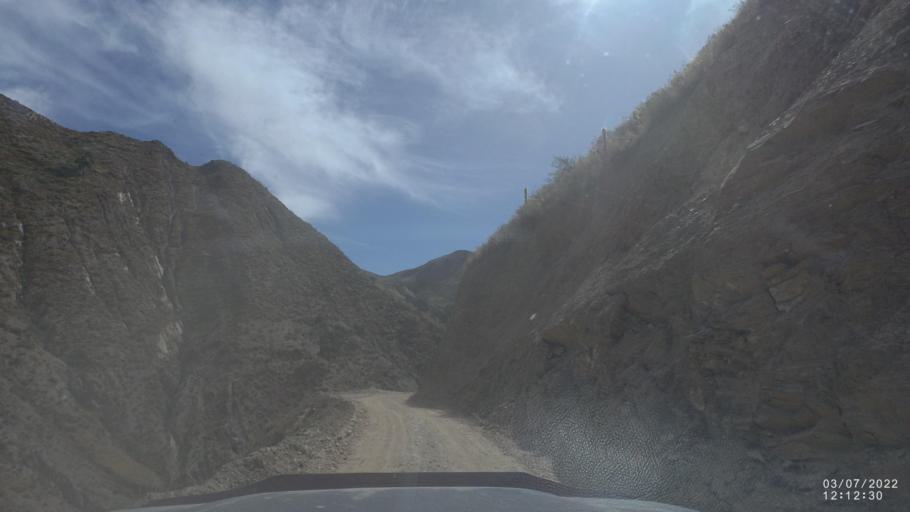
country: BO
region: Cochabamba
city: Irpa Irpa
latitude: -17.8380
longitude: -66.6130
